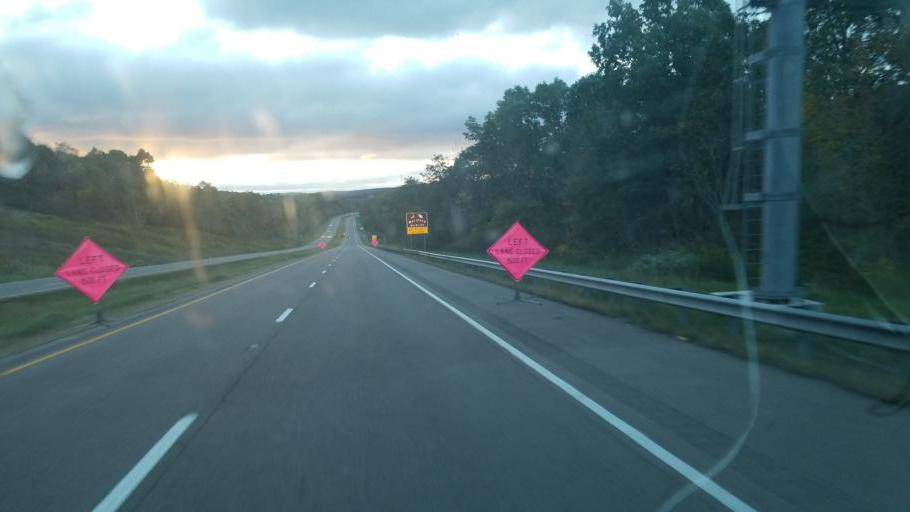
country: US
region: West Virginia
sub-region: Preston County
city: Terra Alta
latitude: 39.6600
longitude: -79.4610
